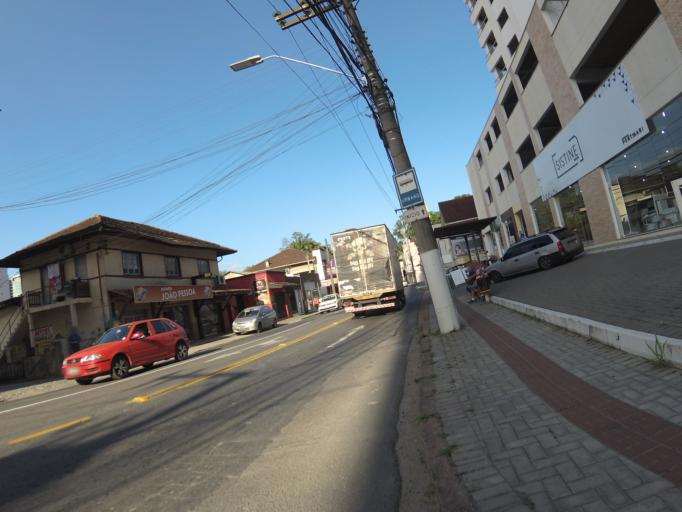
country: BR
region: Santa Catarina
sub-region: Blumenau
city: Blumenau
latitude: -26.9191
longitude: -49.0908
